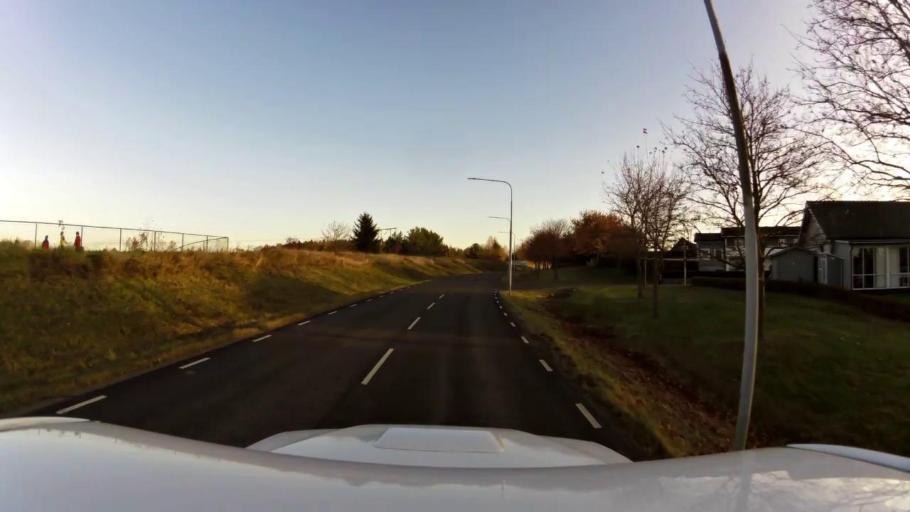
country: SE
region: OEstergoetland
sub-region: Linkopings Kommun
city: Ekangen
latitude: 58.4316
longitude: 15.6778
